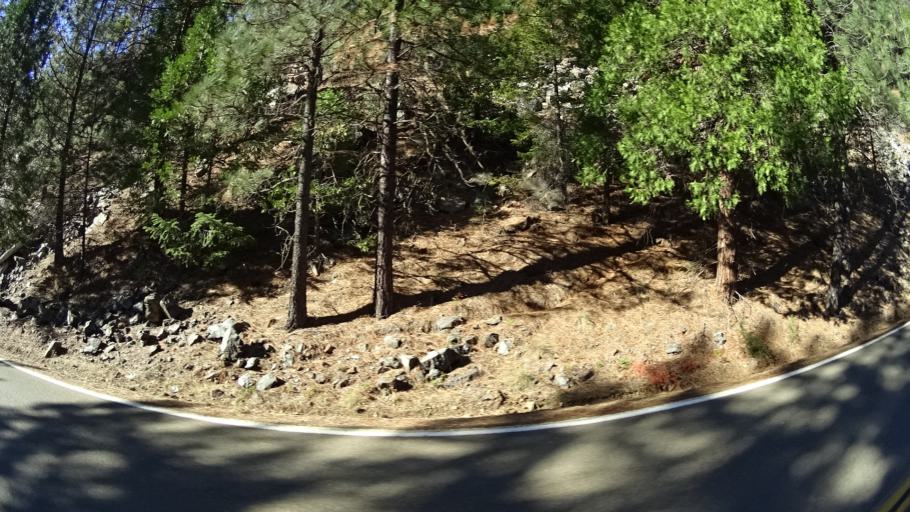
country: US
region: California
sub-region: Trinity County
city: Weaverville
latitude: 41.1498
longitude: -123.1200
